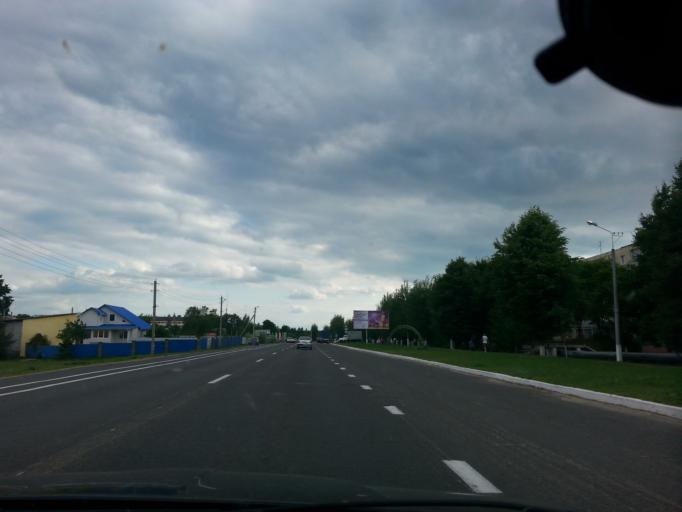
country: BY
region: Minsk
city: Myadzyel
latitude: 54.8702
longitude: 26.9361
